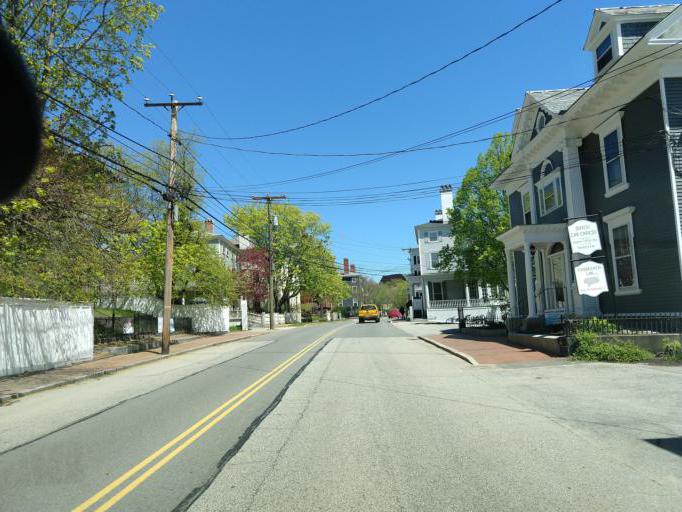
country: US
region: New Hampshire
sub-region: Rockingham County
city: Portsmouth
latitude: 43.0732
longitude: -70.7613
